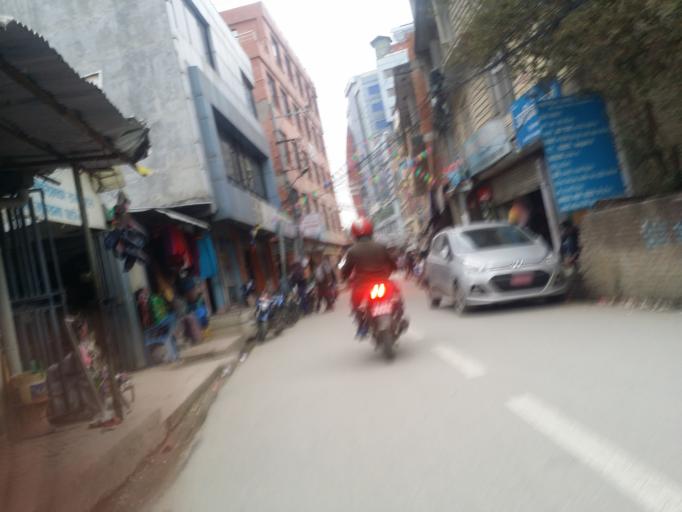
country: NP
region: Central Region
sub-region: Bagmati Zone
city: Kathmandu
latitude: 27.7043
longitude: 85.3481
